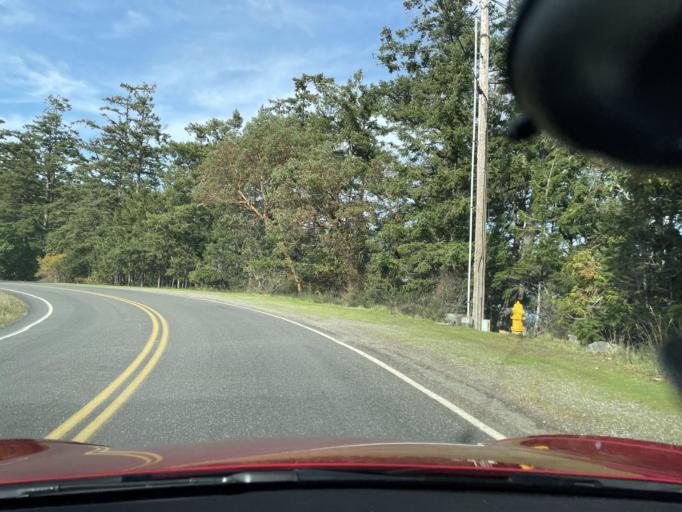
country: US
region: Washington
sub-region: San Juan County
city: Friday Harbor
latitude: 48.5272
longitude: -123.0016
